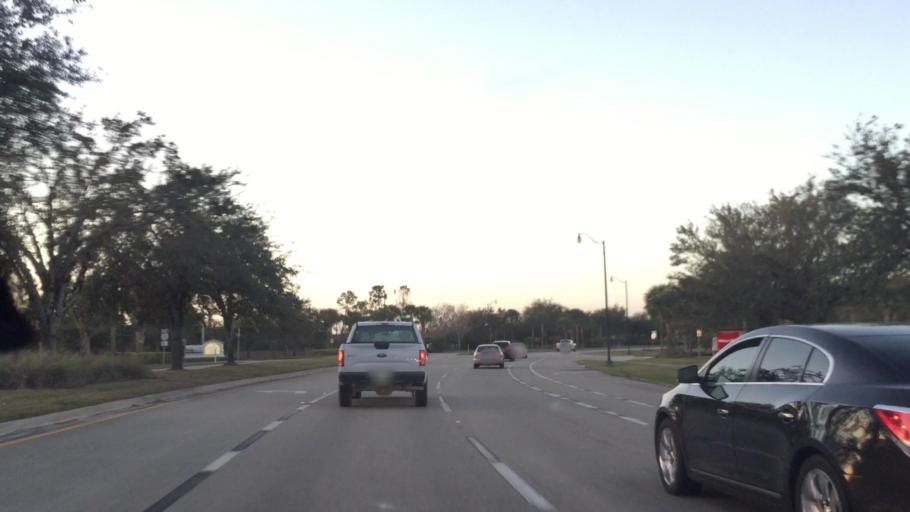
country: US
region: Florida
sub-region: Lee County
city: Gateway
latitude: 26.6117
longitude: -81.7823
